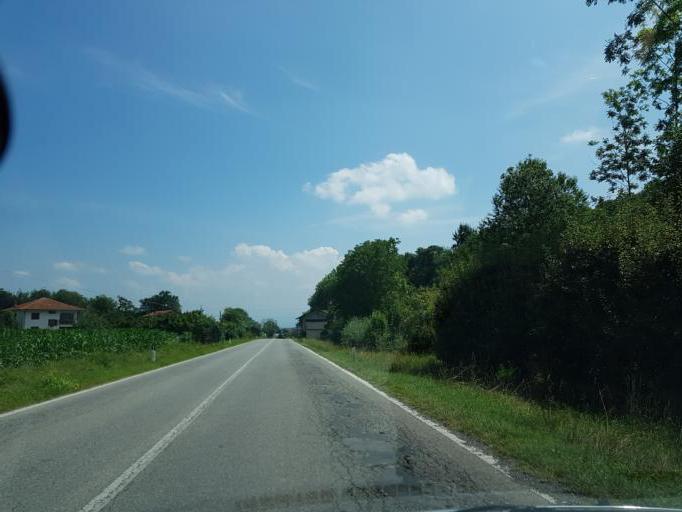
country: IT
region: Piedmont
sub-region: Provincia di Cuneo
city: Montemale di Cuneo
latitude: 44.4435
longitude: 7.4061
